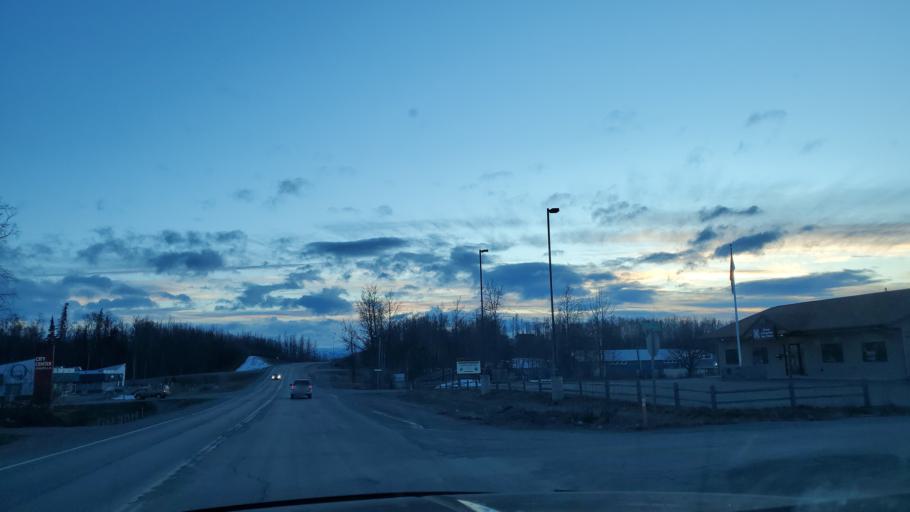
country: US
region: Alaska
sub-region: Matanuska-Susitna Borough
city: Wasilla
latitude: 61.5778
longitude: -149.4415
